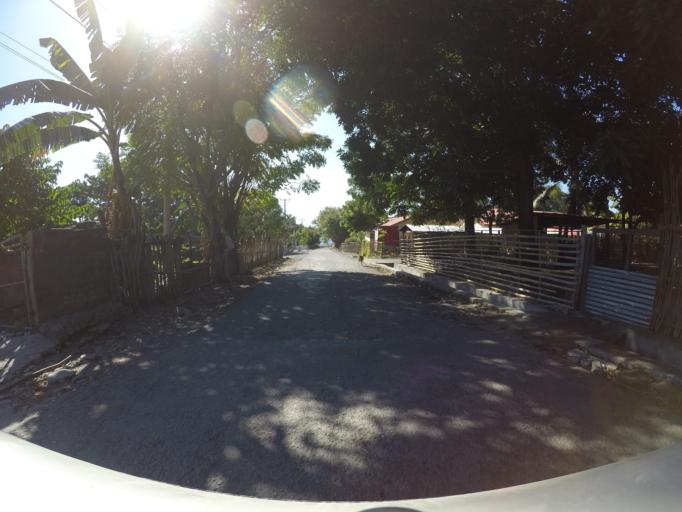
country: TL
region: Liquica
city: Maubara
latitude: -8.6121
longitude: 125.2054
